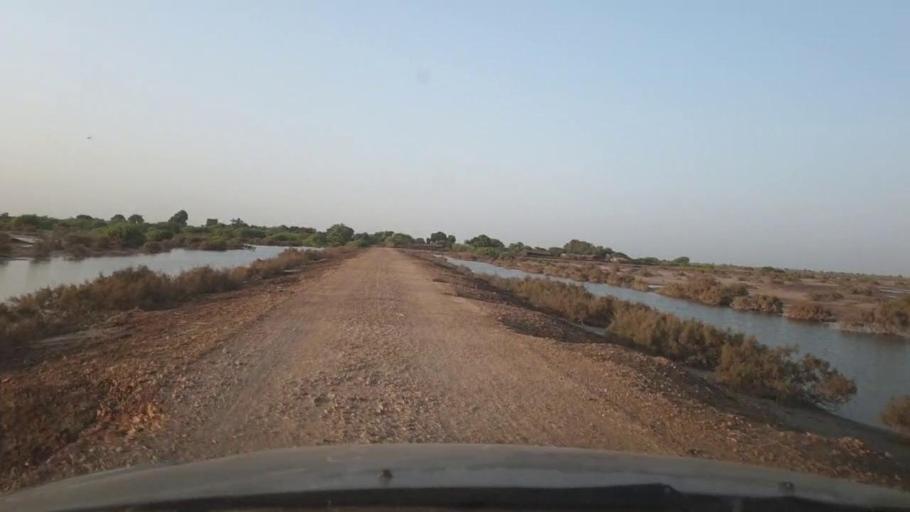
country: PK
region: Sindh
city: Tando Ghulam Ali
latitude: 25.1661
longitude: 68.9748
